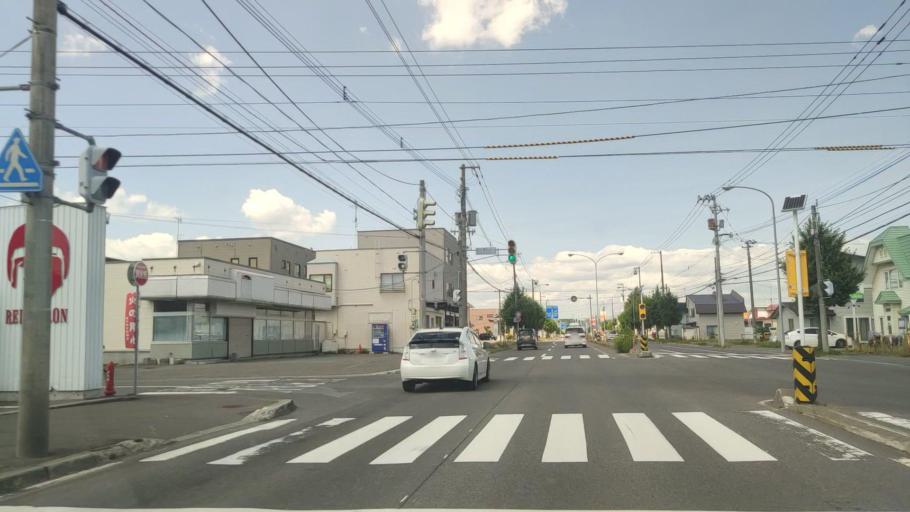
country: JP
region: Hokkaido
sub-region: Asahikawa-shi
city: Asahikawa
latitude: 43.8013
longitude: 142.3916
